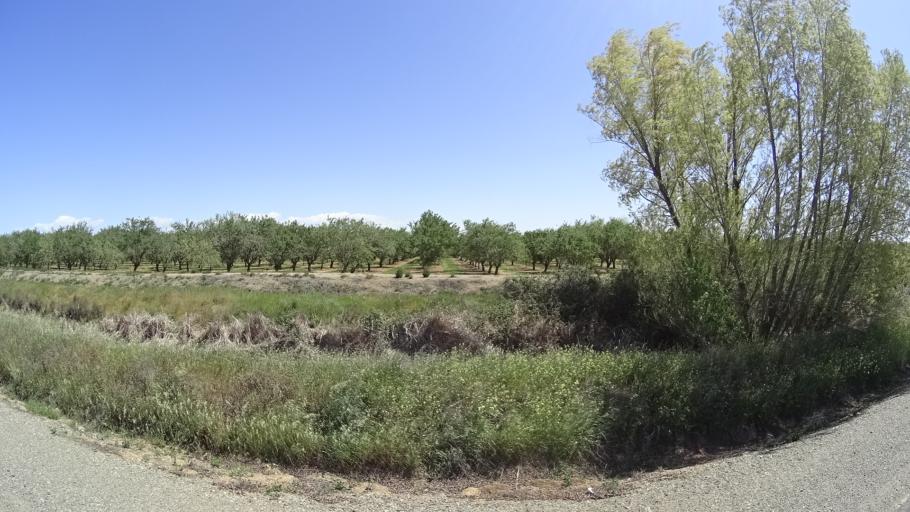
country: US
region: California
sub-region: Glenn County
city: Orland
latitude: 39.7907
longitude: -122.1410
